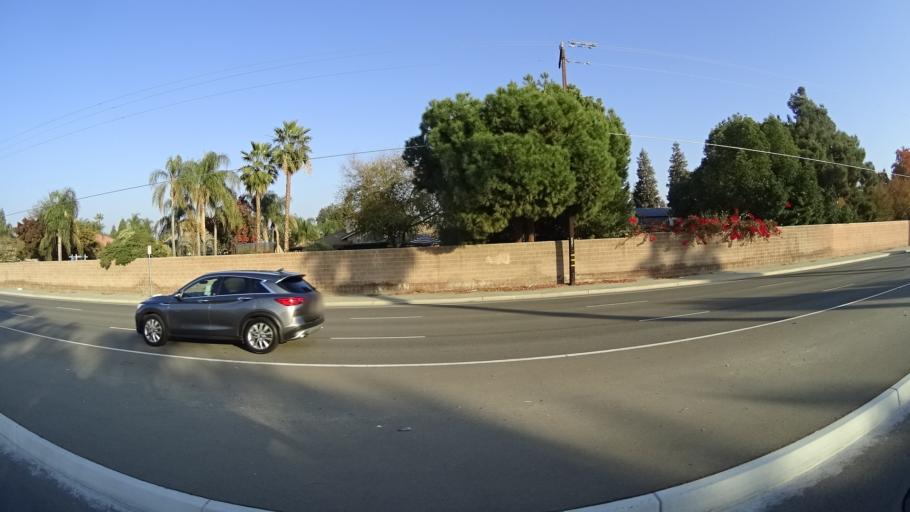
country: US
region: California
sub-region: Kern County
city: Rosedale
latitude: 35.3774
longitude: -119.1456
